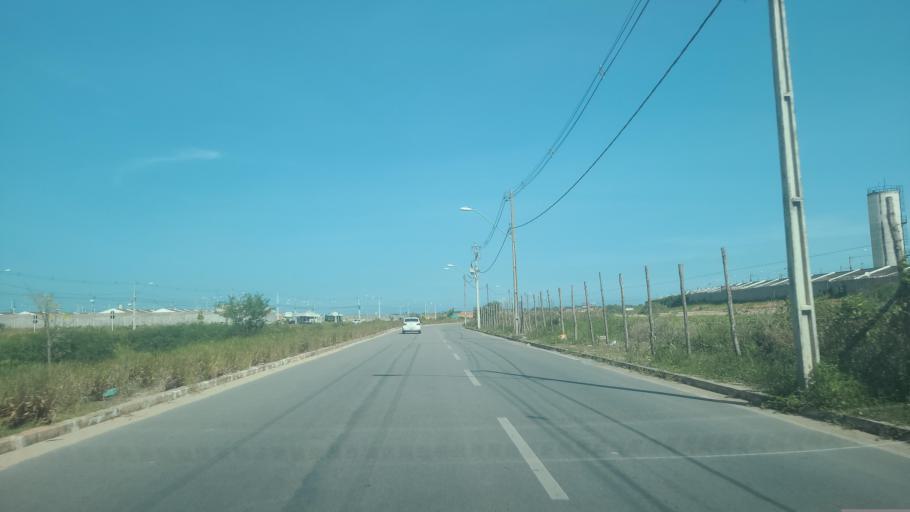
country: BR
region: Alagoas
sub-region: Satuba
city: Satuba
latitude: -9.5316
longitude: -35.7724
